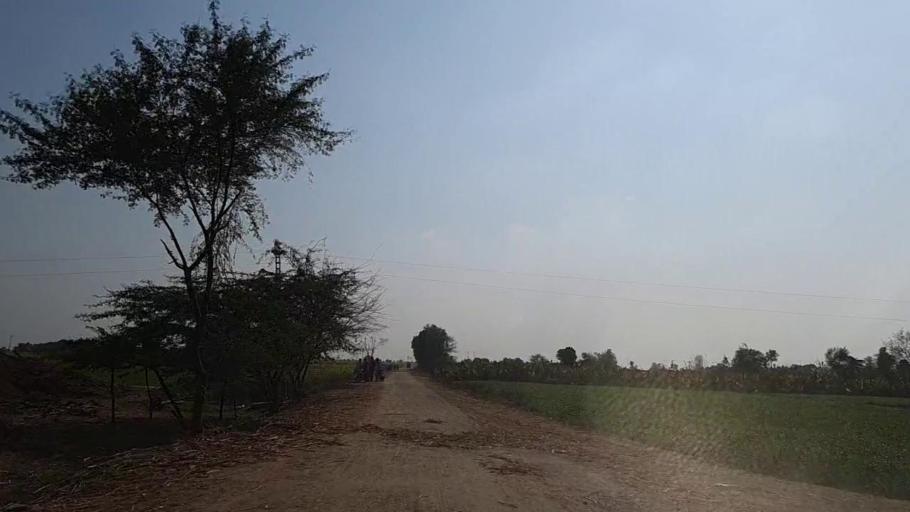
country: PK
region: Sindh
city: Daur
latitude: 26.4234
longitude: 68.2368
